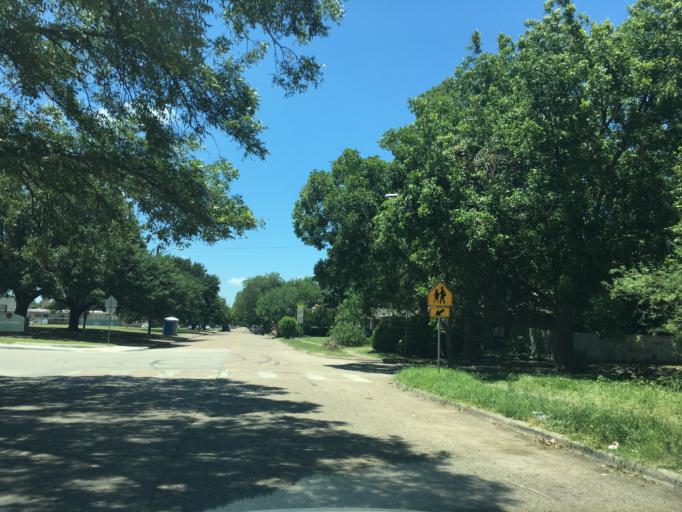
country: US
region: Texas
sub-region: Dallas County
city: Garland
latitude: 32.8484
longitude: -96.6747
